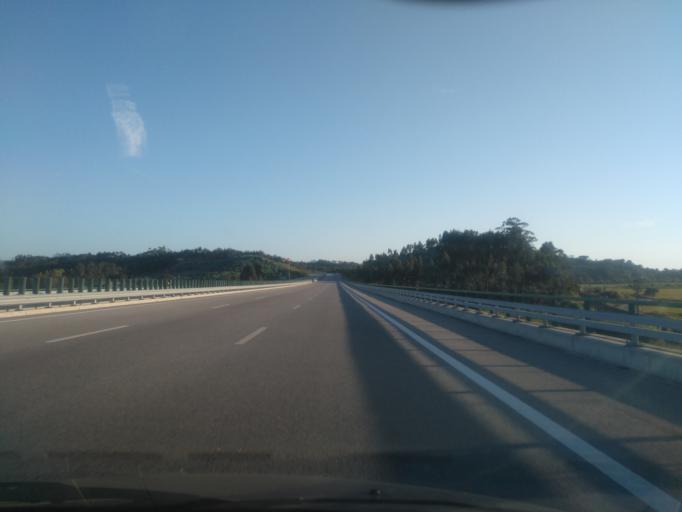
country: PT
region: Coimbra
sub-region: Figueira da Foz
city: Alhadas
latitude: 40.1288
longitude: -8.7449
